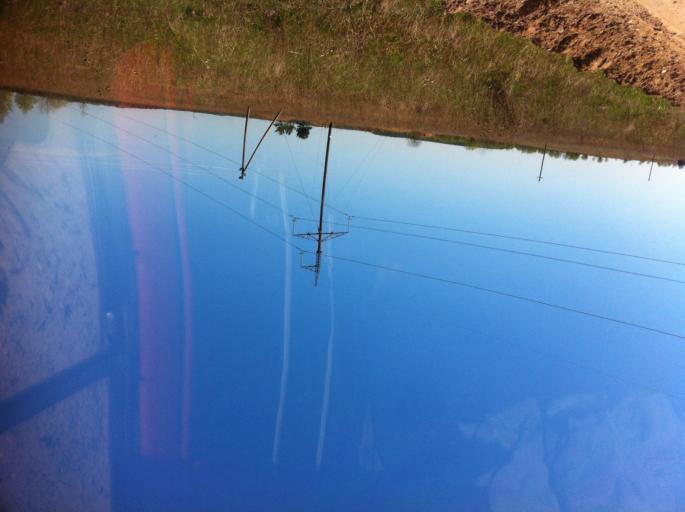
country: RU
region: Pskov
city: Izborsk
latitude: 57.8322
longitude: 27.9834
